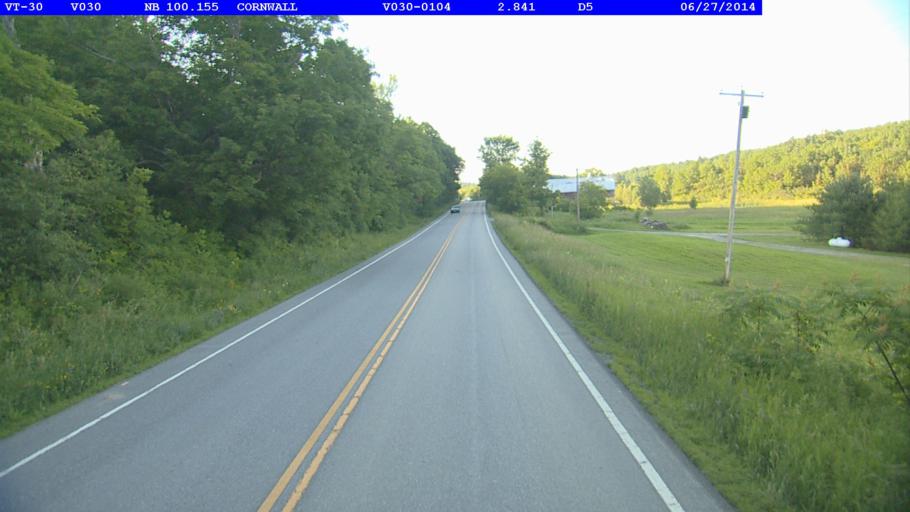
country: US
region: Vermont
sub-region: Addison County
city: Middlebury (village)
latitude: 43.9486
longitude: -73.2106
